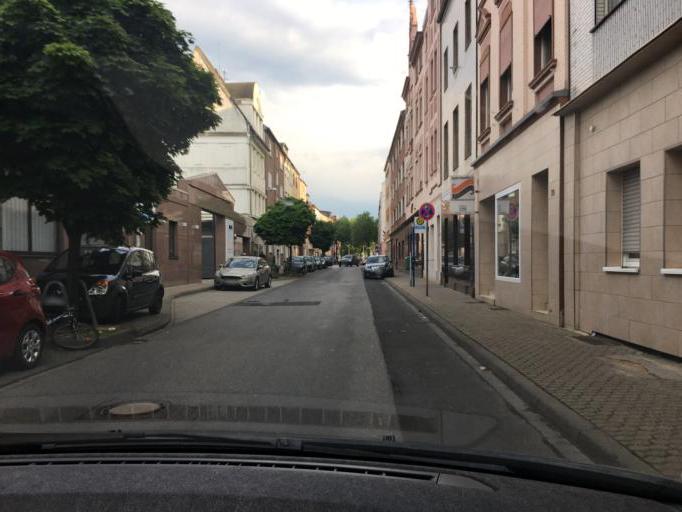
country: DE
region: North Rhine-Westphalia
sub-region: Regierungsbezirk Koln
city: Dueren
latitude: 50.8124
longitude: 6.4778
